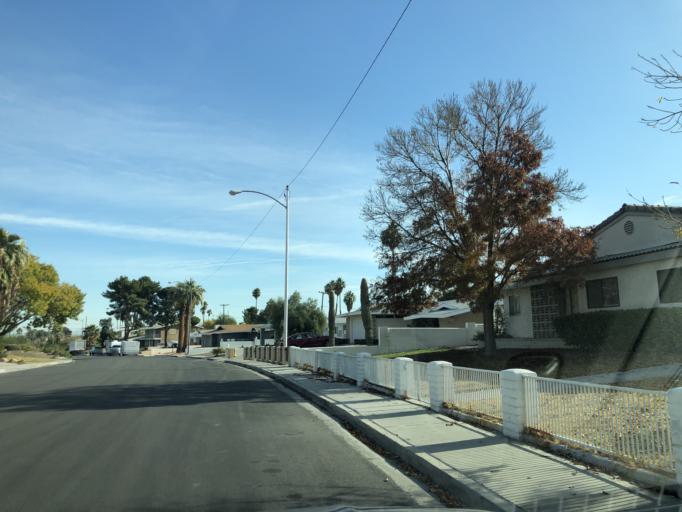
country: US
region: Nevada
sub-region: Clark County
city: Winchester
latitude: 36.1232
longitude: -115.1319
